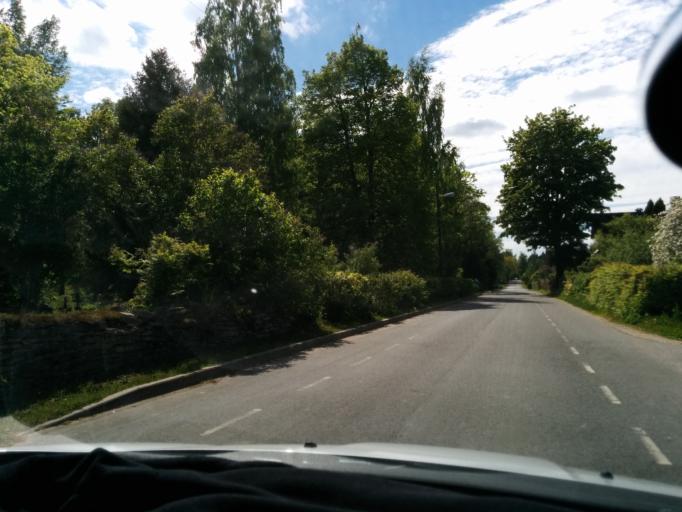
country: EE
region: Harju
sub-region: Loksa linn
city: Loksa
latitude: 59.5754
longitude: 25.7223
